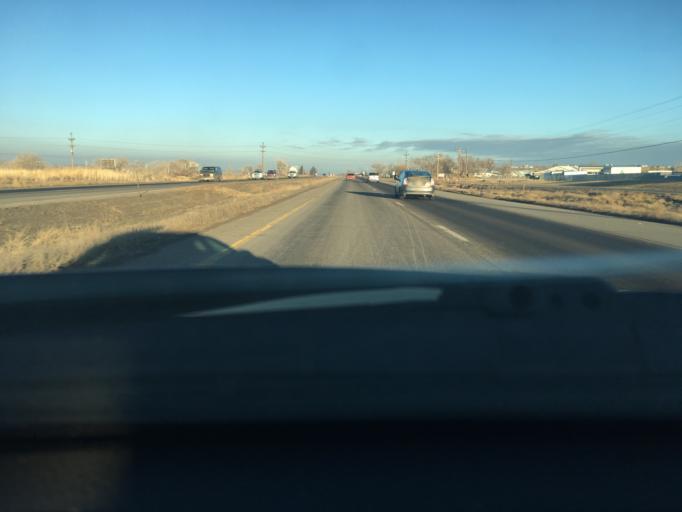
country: US
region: Colorado
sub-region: Montrose County
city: Montrose
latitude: 38.5091
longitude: -107.9103
